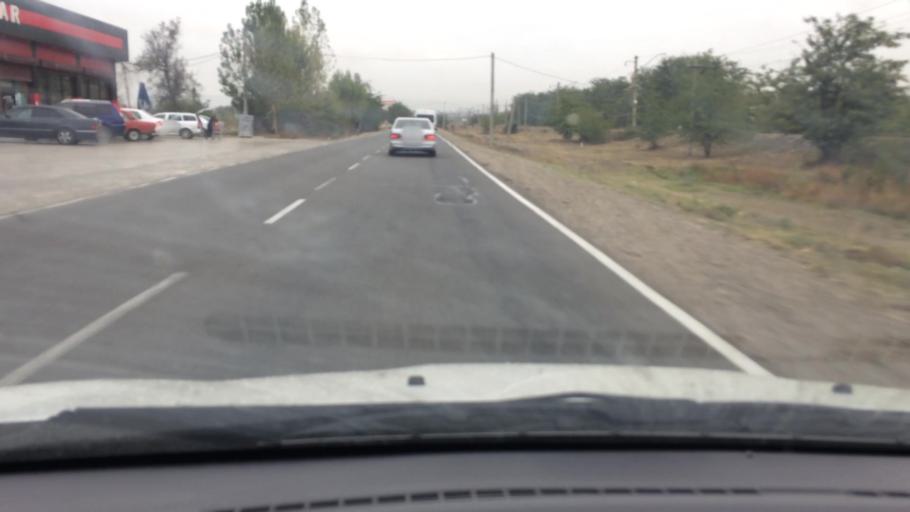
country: GE
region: Kvemo Kartli
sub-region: Marneuli
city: Marneuli
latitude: 41.4537
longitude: 44.8126
